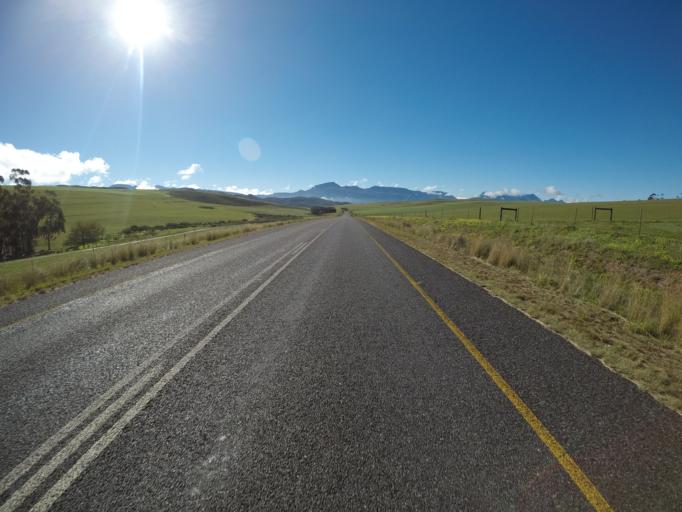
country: ZA
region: Western Cape
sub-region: Overberg District Municipality
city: Caledon
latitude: -34.1217
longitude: 19.5169
